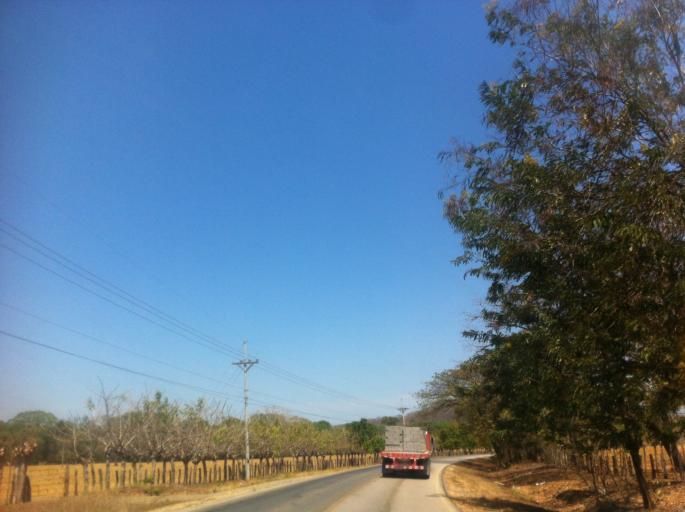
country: CR
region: Guanacaste
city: Santa Cruz
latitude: 10.2260
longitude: -85.5458
